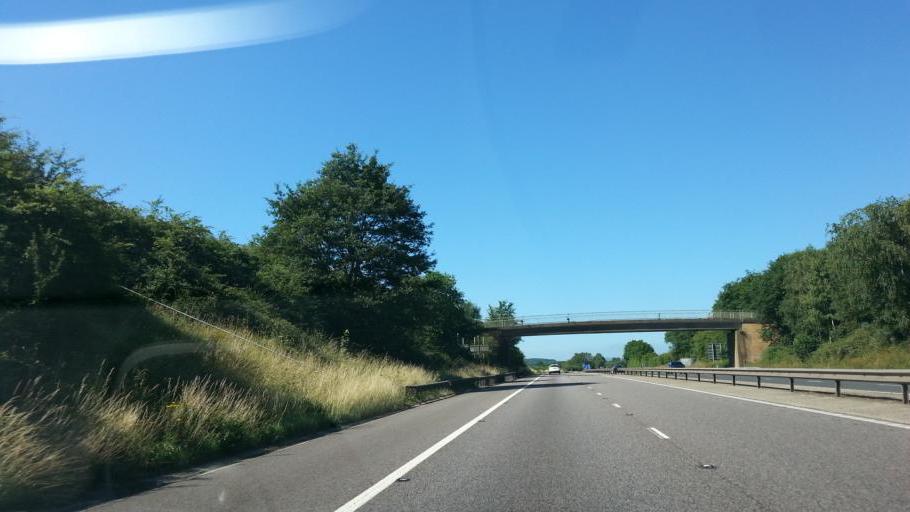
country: GB
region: England
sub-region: Worcestershire
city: Bredon
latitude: 52.0397
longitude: -2.1529
